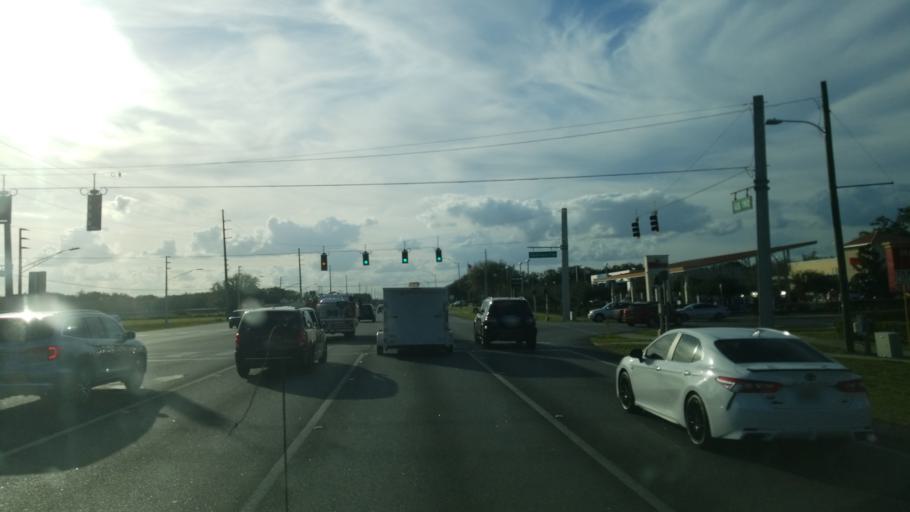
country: US
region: Florida
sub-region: Osceola County
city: Saint Cloud
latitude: 28.2461
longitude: -81.2556
